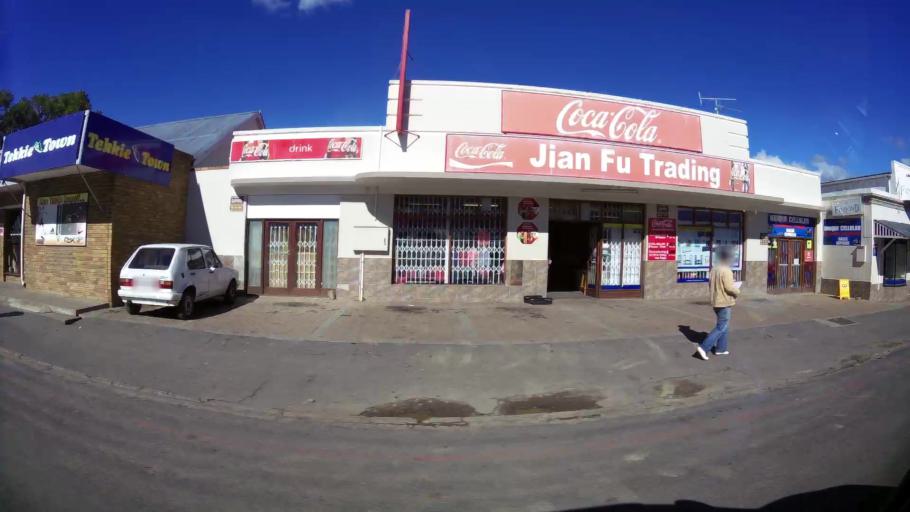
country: ZA
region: Western Cape
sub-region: Cape Winelands District Municipality
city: Ashton
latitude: -33.8065
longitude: 19.8824
